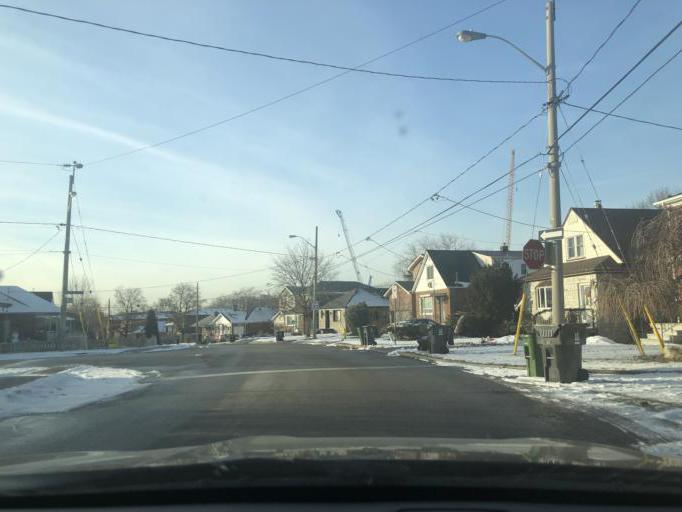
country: CA
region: Ontario
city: Toronto
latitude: 43.6965
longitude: -79.4706
